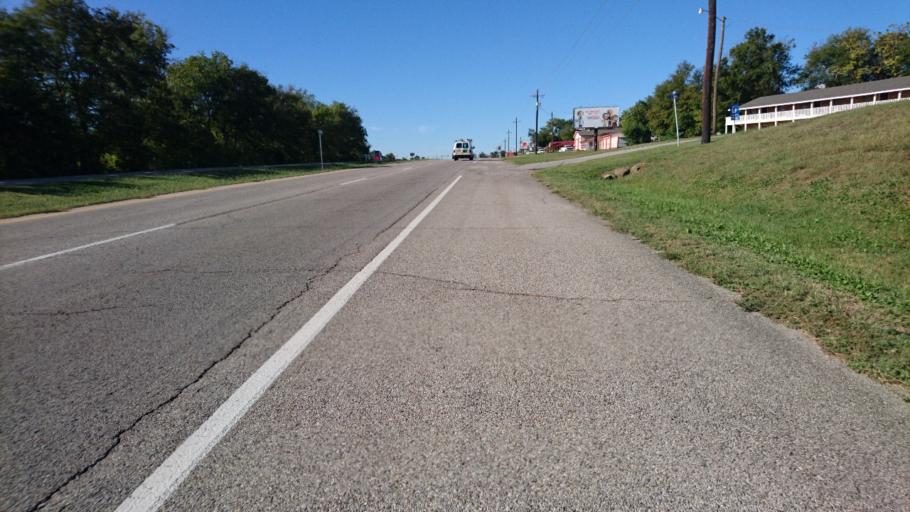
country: US
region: Oklahoma
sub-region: Rogers County
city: Catoosa
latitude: 36.1849
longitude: -95.7444
